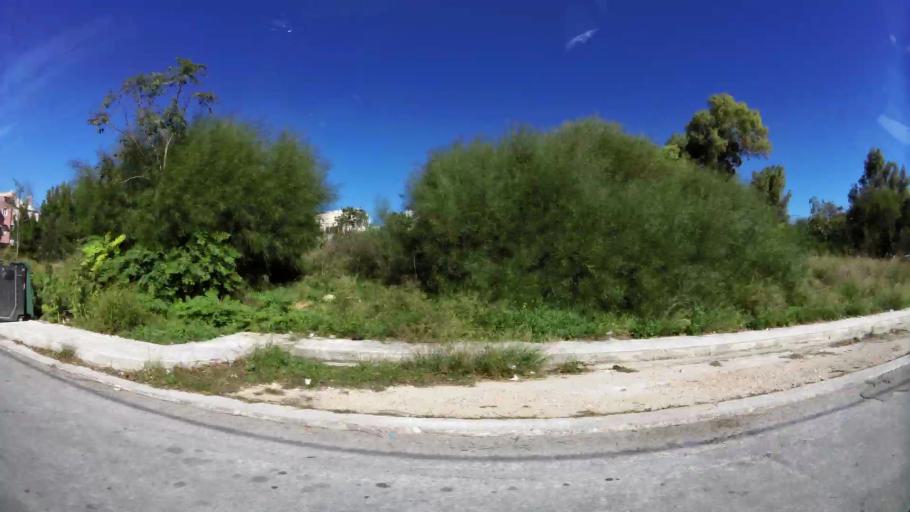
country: GR
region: Attica
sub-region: Nomarchia Anatolikis Attikis
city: Gerakas
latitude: 38.0069
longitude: 23.8567
